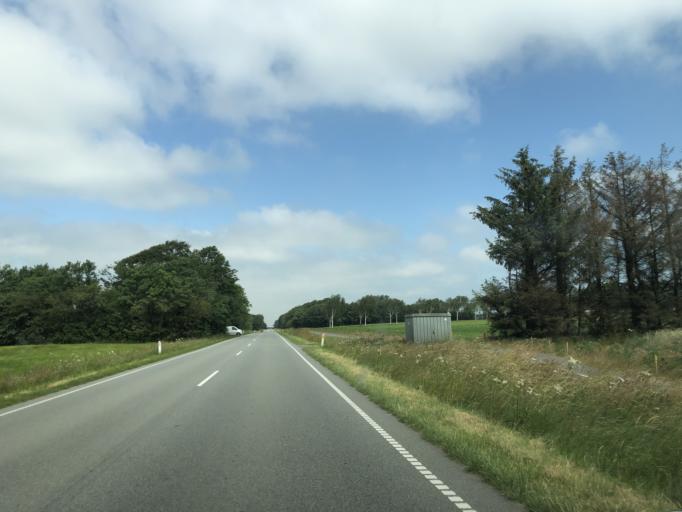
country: DK
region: South Denmark
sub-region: Varde Kommune
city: Varde
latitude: 55.6452
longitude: 8.4872
